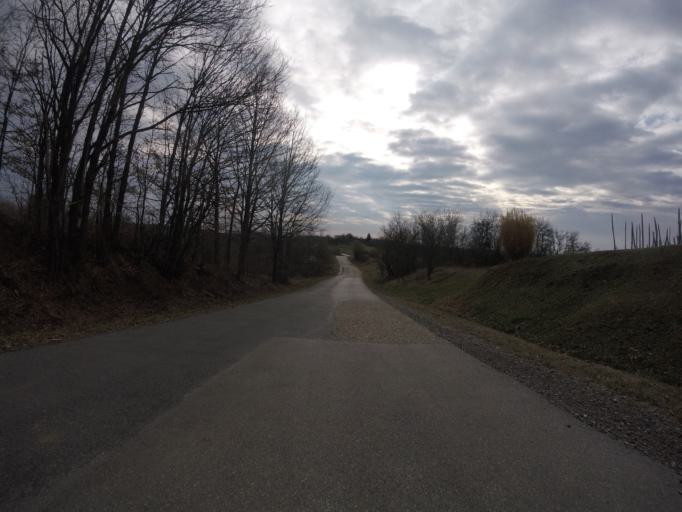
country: HR
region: Zagrebacka
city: Mraclin
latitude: 45.5171
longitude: 16.0510
